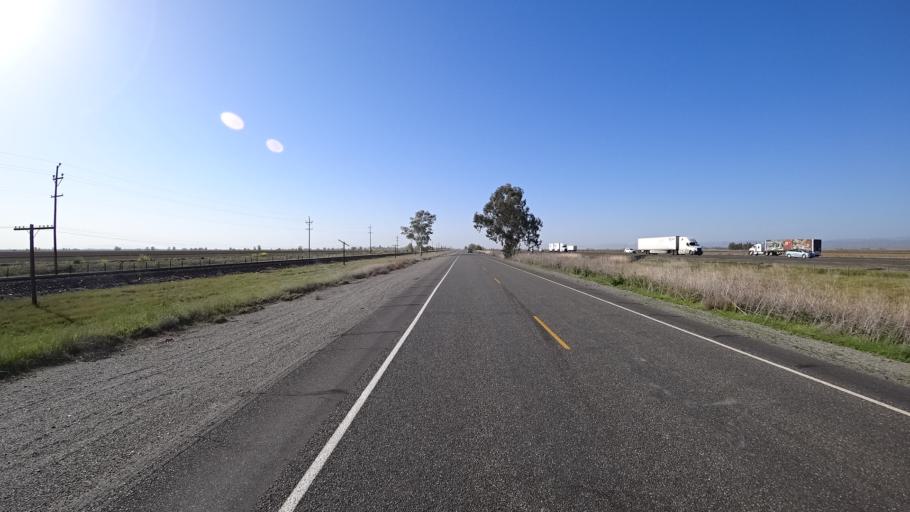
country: US
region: California
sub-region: Glenn County
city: Willows
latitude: 39.4571
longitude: -122.1929
